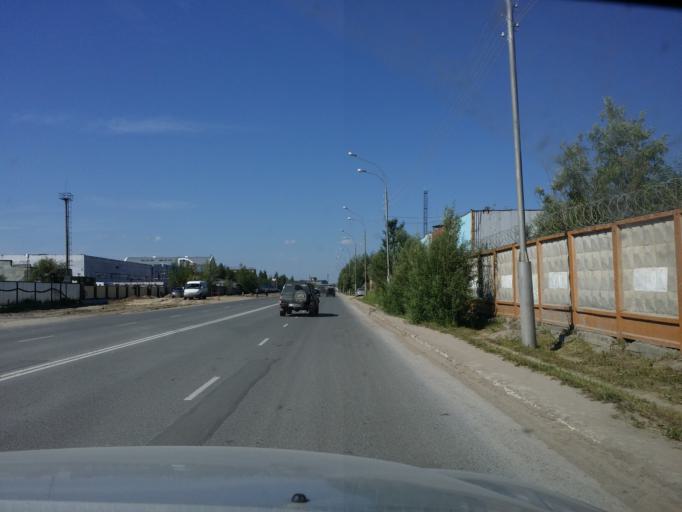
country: RU
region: Khanty-Mansiyskiy Avtonomnyy Okrug
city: Nizhnevartovsk
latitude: 60.9415
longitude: 76.5489
